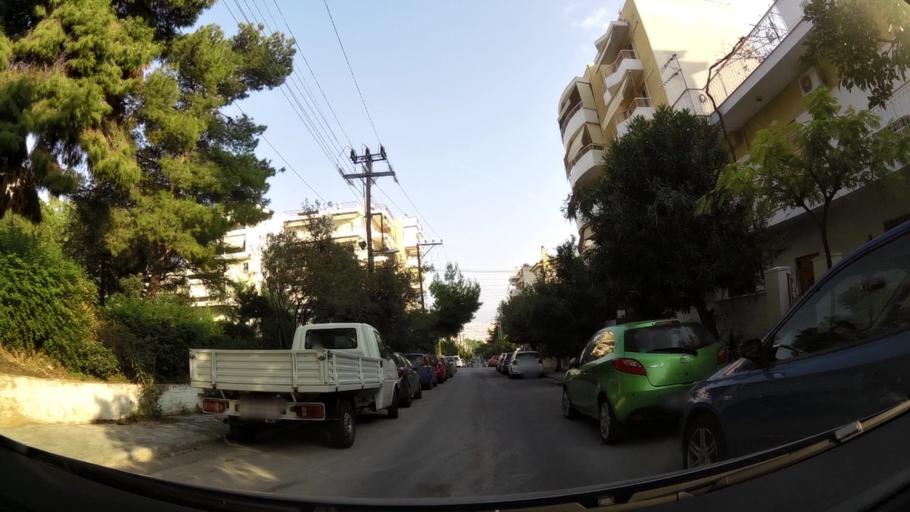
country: GR
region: Attica
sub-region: Nomarchia Athinas
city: Petroupolis
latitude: 38.0467
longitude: 23.6806
